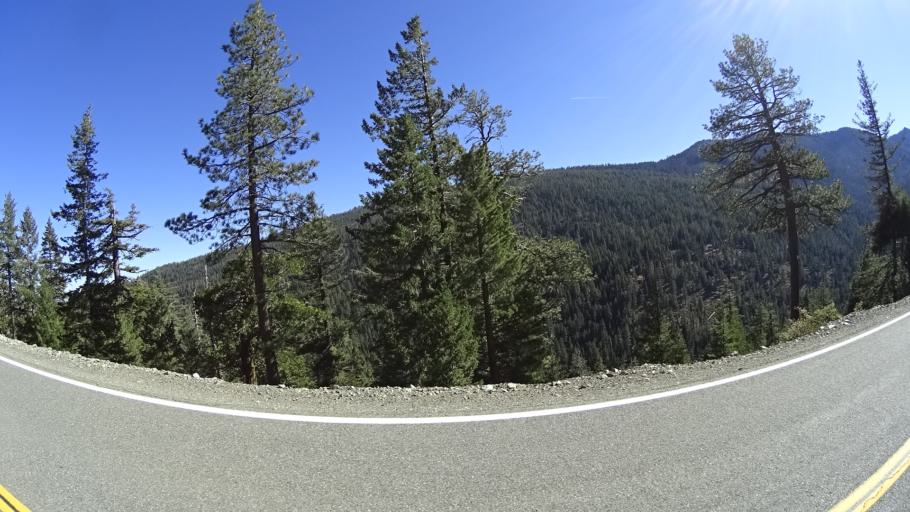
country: US
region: California
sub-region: Trinity County
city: Weaverville
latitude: 41.2369
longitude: -122.8927
